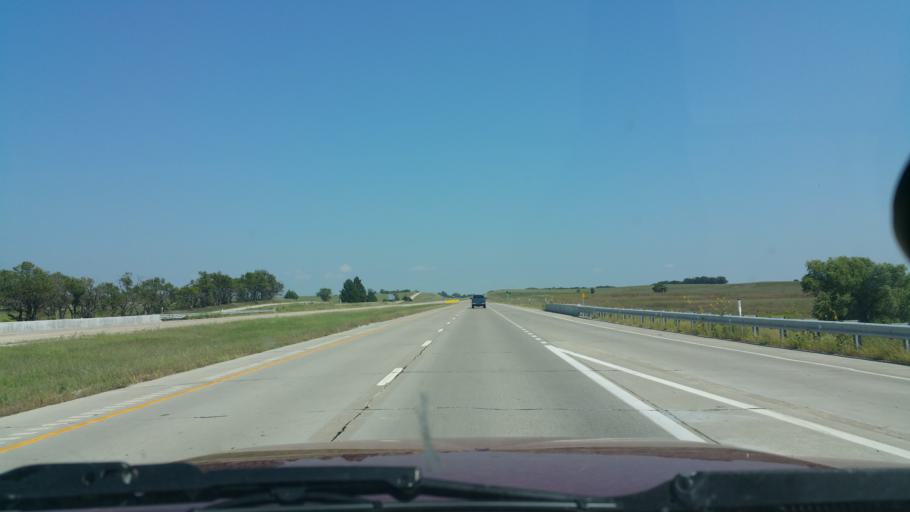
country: US
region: Kansas
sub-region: Dickinson County
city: Abilene
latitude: 38.9438
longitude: -97.1648
